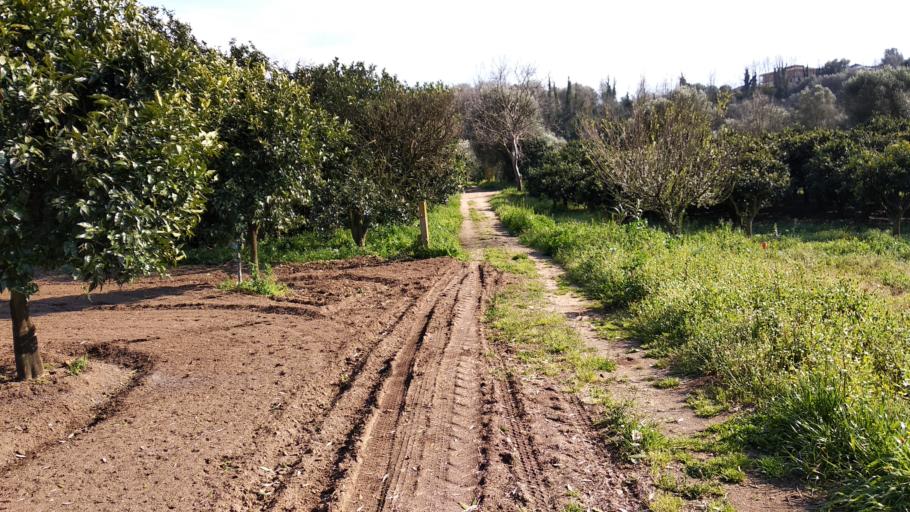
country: IT
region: Calabria
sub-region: Provincia di Reggio Calabria
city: Rizziconi
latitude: 38.4309
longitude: 15.9595
